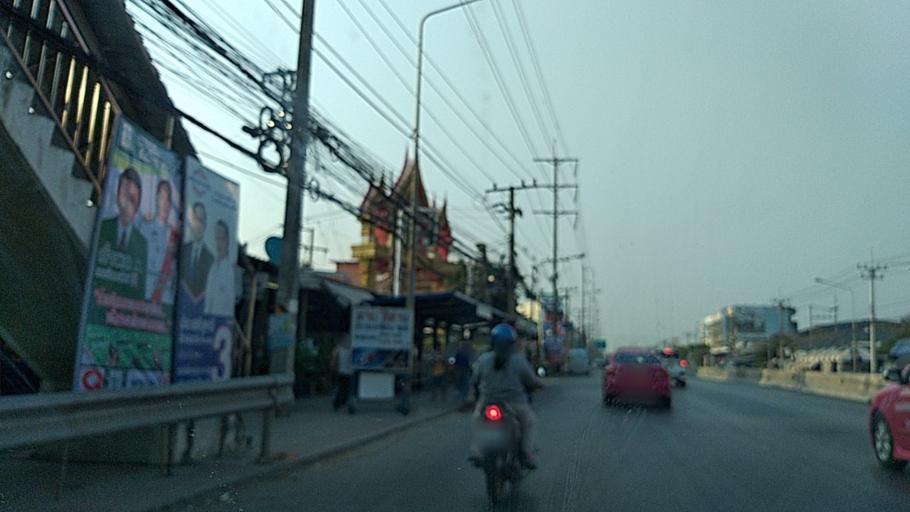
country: TH
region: Phra Nakhon Si Ayutthaya
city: Ban Bang Kadi Pathum Thani
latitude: 13.9997
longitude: 100.5556
